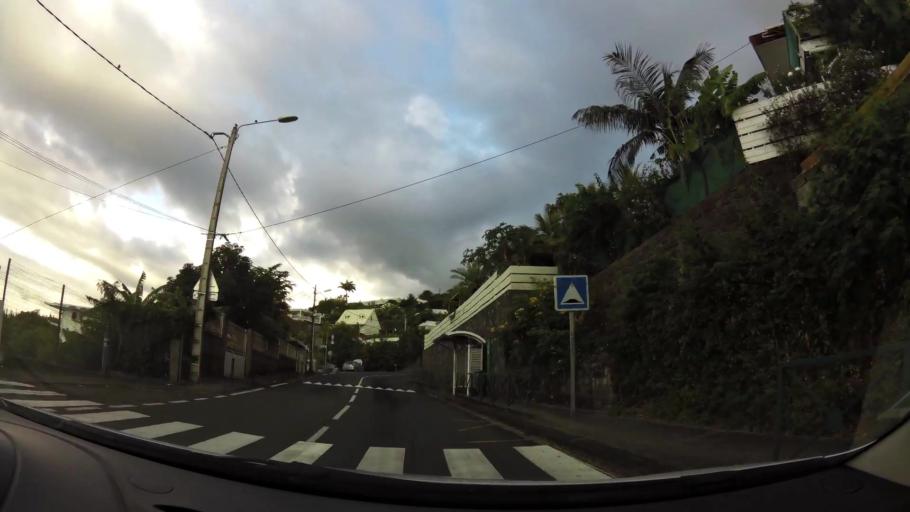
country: RE
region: Reunion
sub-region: Reunion
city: Saint-Denis
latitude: -20.9004
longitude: 55.4445
